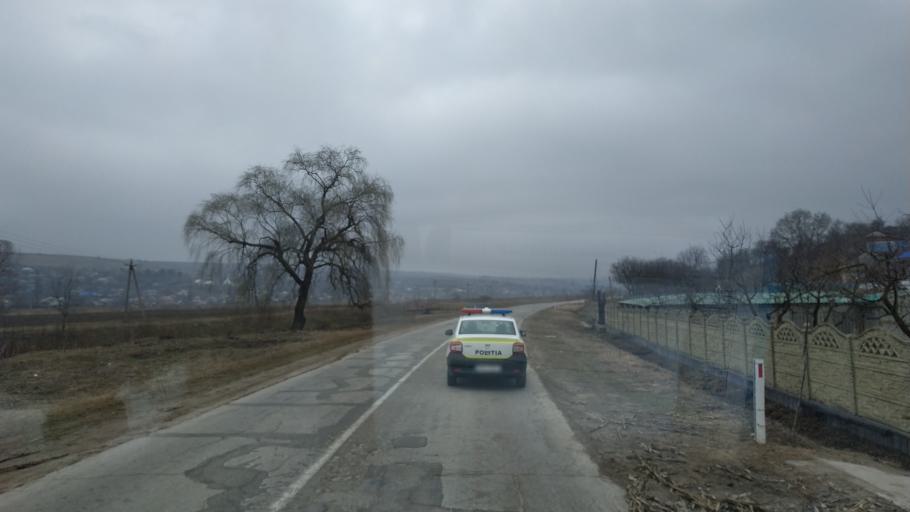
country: MD
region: Hincesti
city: Hincesti
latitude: 46.9765
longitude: 28.4683
